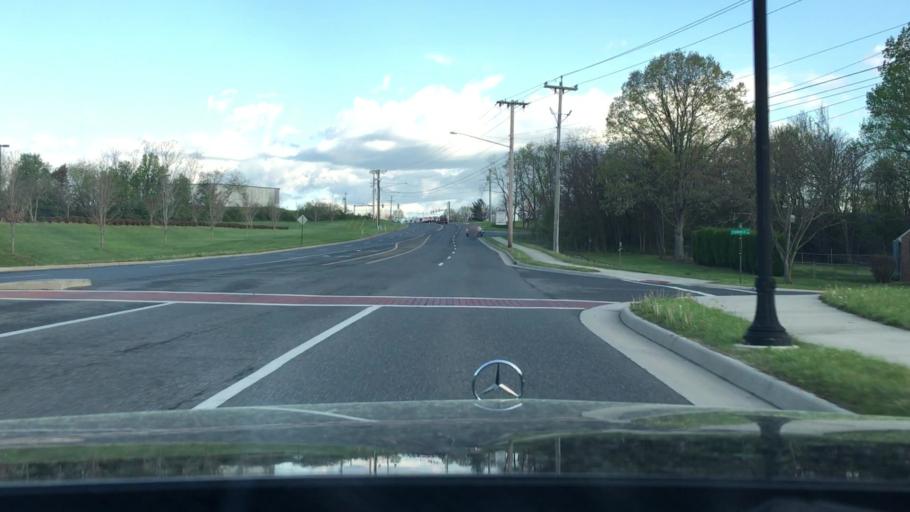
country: US
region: Virginia
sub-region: Campbell County
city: Timberlake
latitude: 37.3425
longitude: -79.2320
